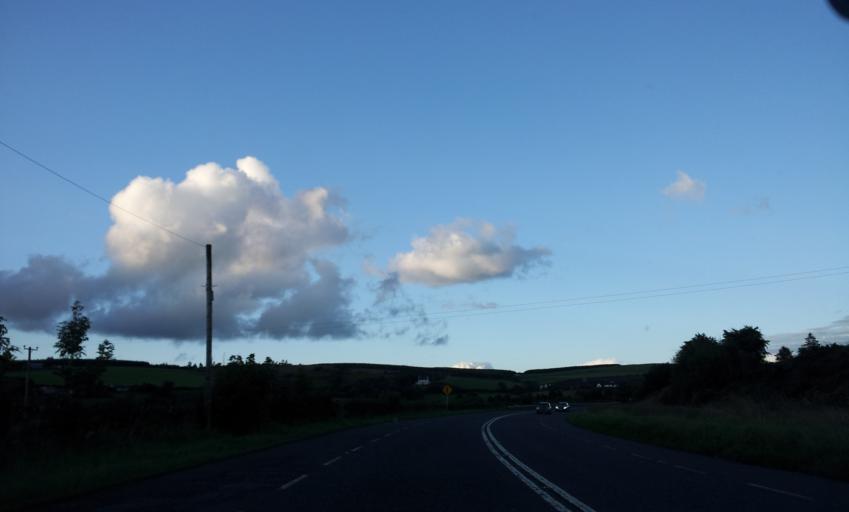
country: IE
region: Munster
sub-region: County Limerick
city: Newcastle West
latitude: 52.4135
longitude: -9.1539
